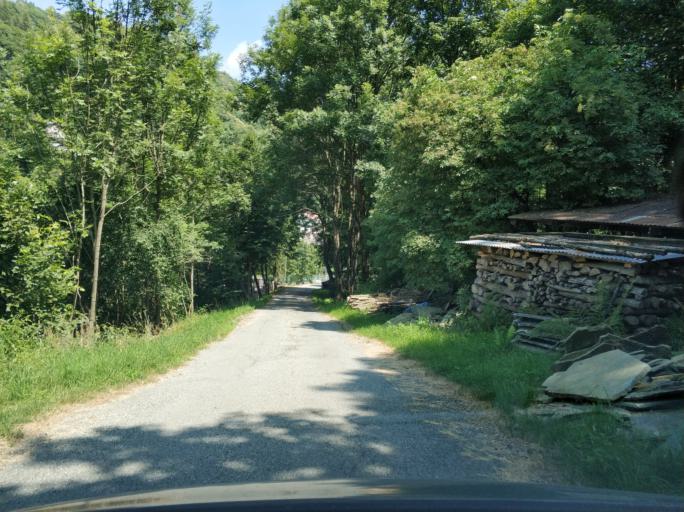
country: IT
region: Piedmont
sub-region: Provincia di Torino
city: Ceres
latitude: 45.3147
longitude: 7.3775
